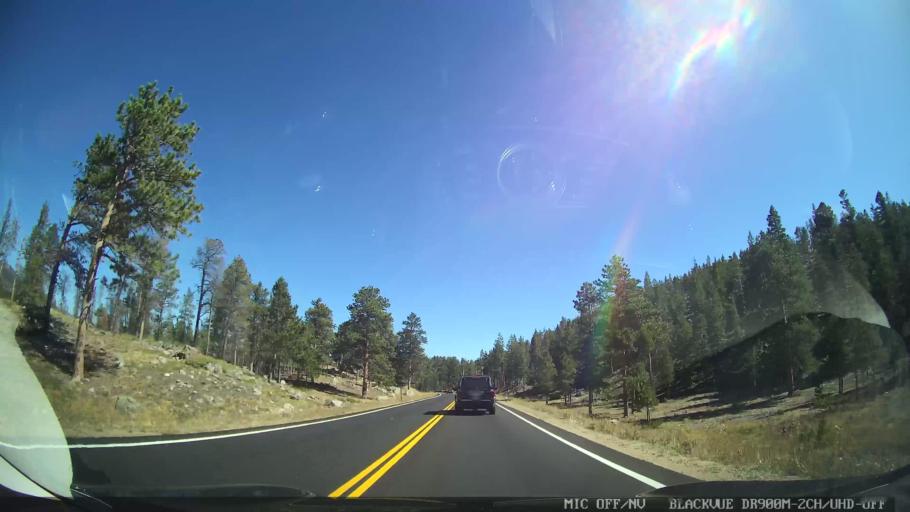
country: US
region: Colorado
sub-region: Larimer County
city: Estes Park
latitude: 40.3398
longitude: -105.5995
